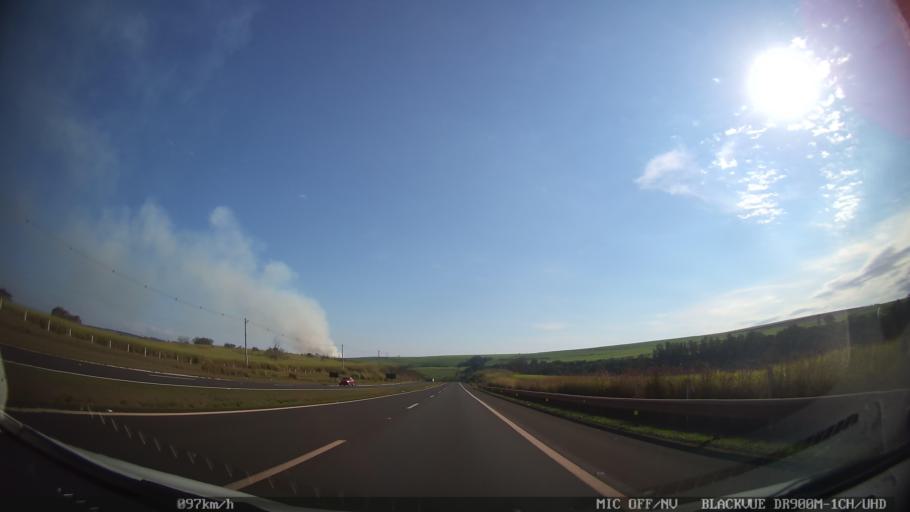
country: BR
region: Sao Paulo
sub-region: Piracicaba
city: Piracicaba
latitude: -22.6822
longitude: -47.5738
